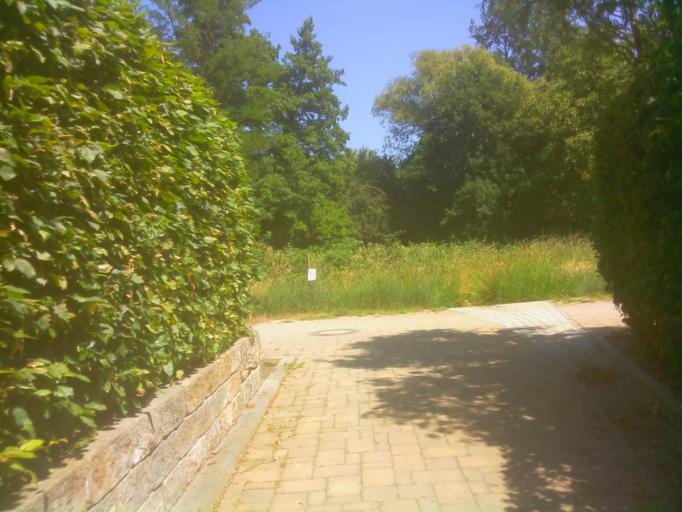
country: DE
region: Hesse
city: Lorsch
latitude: 49.6499
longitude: 8.5751
